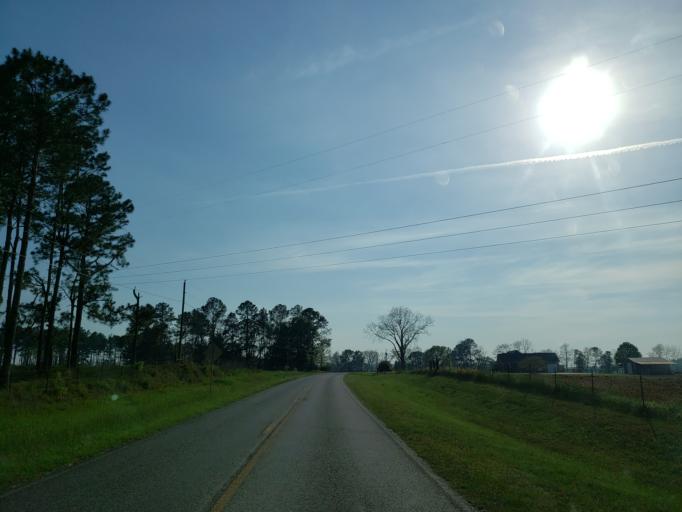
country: US
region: Georgia
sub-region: Tift County
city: Tifton
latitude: 31.5337
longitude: -83.5557
